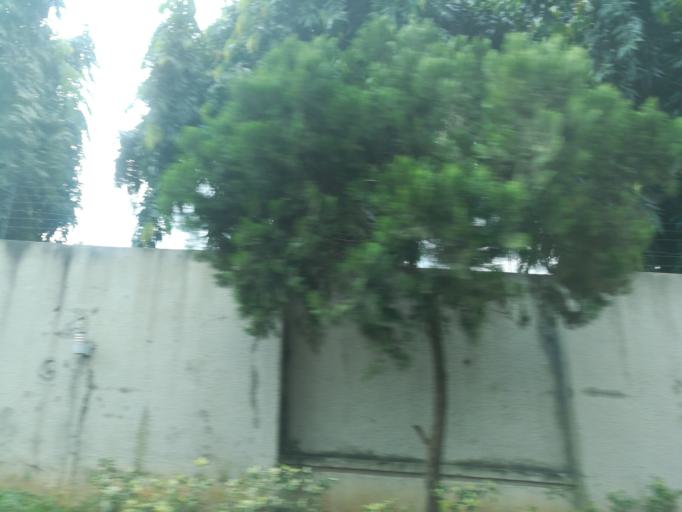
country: NG
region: Lagos
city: Oshodi
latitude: 6.5719
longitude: 3.3539
